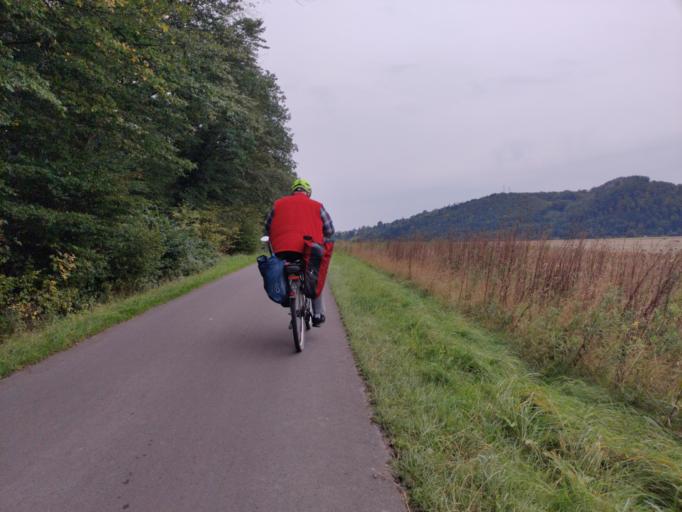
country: DE
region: Lower Saxony
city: Brevorde
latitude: 51.9060
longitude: 9.4277
